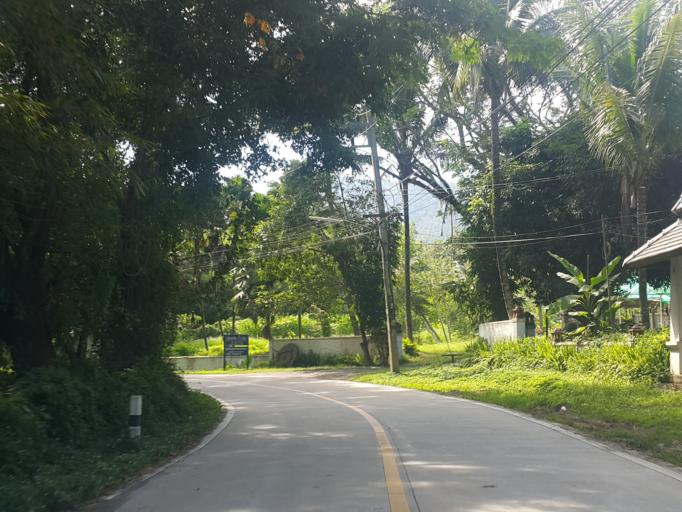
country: TH
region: Chiang Mai
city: Mae On
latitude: 18.8155
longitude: 99.2252
